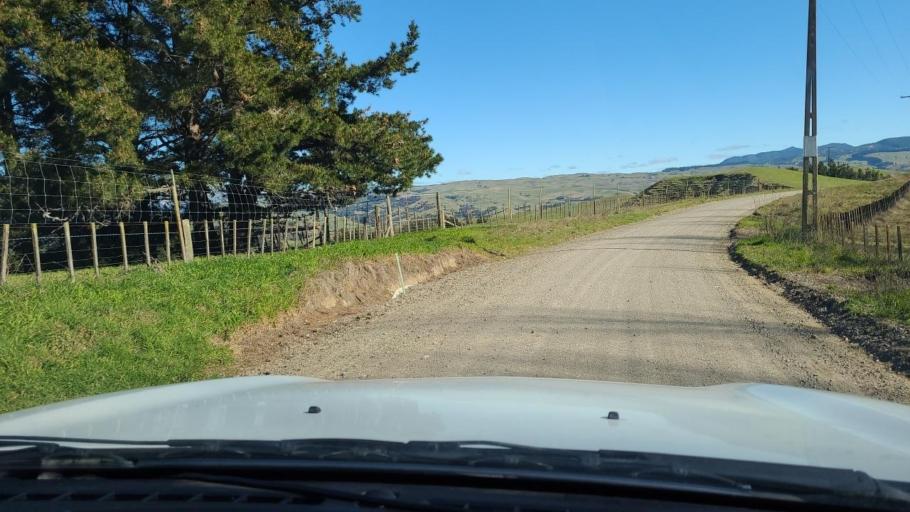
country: NZ
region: Hawke's Bay
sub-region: Napier City
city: Taradale
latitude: -39.4936
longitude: 176.4827
